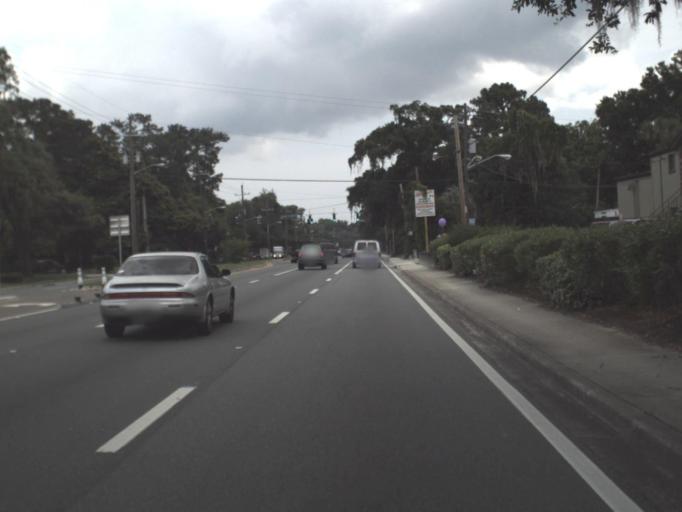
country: US
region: Florida
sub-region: Duval County
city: Jacksonville
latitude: 30.3091
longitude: -81.6154
